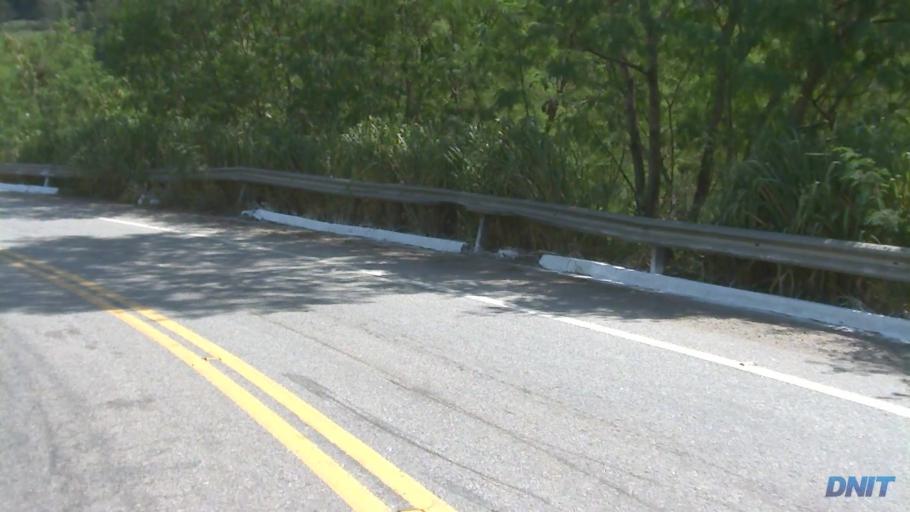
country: BR
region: Minas Gerais
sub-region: Timoteo
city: Timoteo
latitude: -19.5398
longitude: -42.6867
